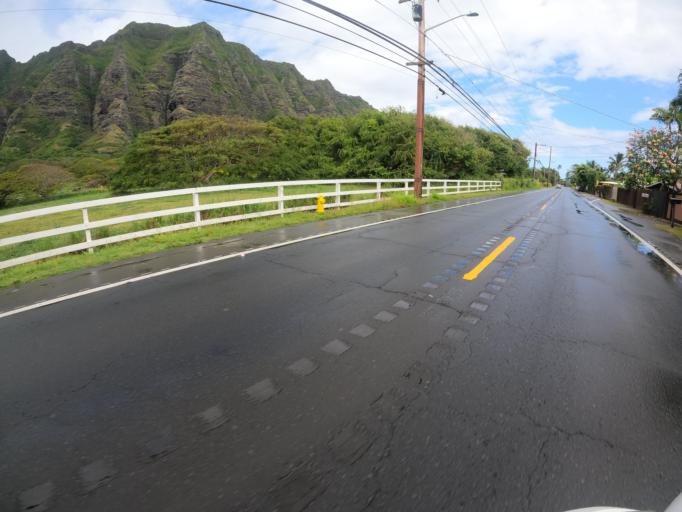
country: US
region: Hawaii
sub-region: Honolulu County
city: Ka'a'awa
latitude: 21.5235
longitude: -157.8355
